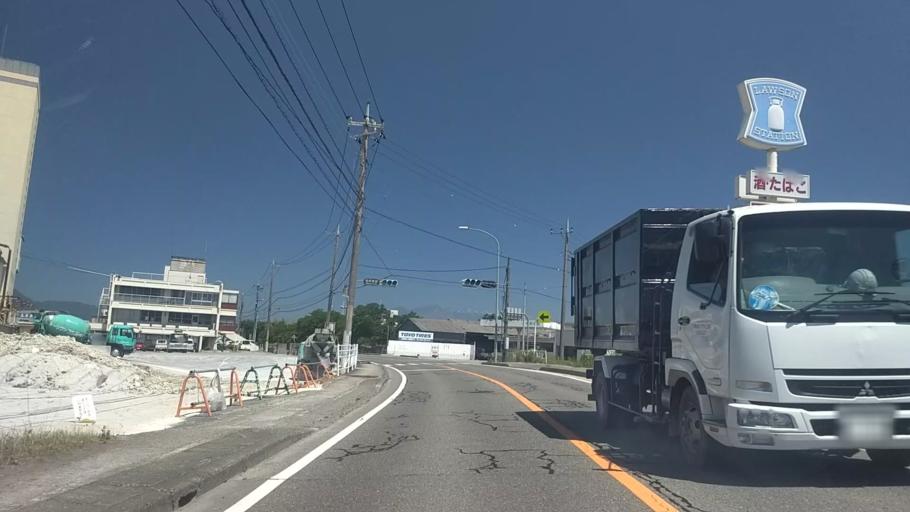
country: JP
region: Yamanashi
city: Nirasaki
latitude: 35.6907
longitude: 138.4609
